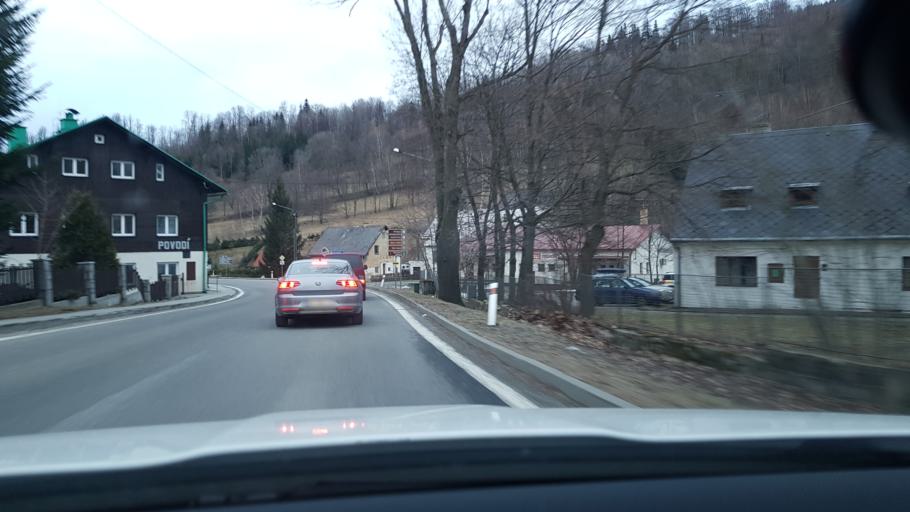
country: CZ
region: Olomoucky
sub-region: Okres Jesenik
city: Jesenik
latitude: 50.1618
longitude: 17.1953
